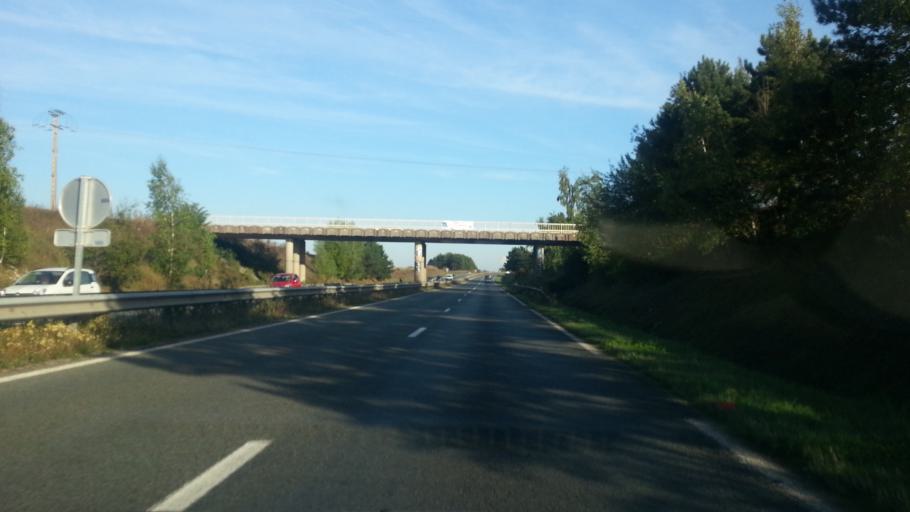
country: FR
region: Picardie
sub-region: Departement de l'Oise
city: Warluis
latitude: 49.4221
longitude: 2.1537
